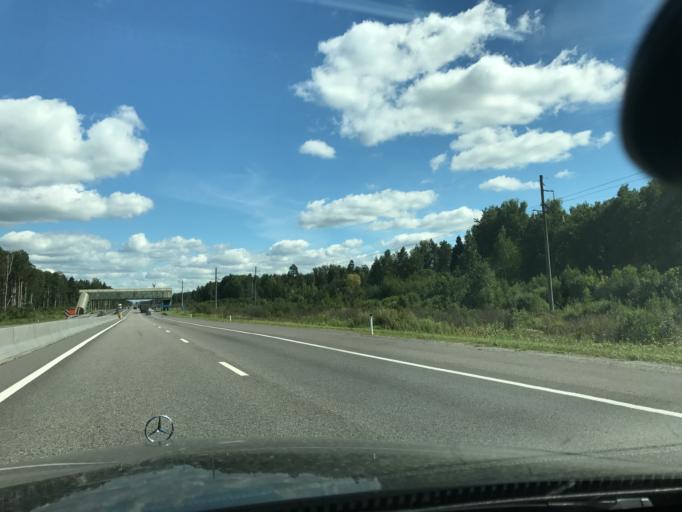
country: RU
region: Nizjnij Novgorod
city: Smolino
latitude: 56.2815
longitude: 43.0867
